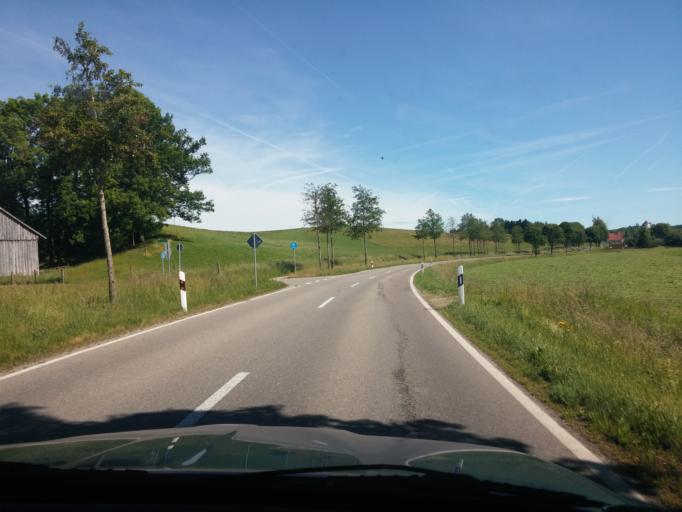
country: DE
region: Bavaria
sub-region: Swabia
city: Woringen
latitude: 47.8952
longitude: 10.2091
